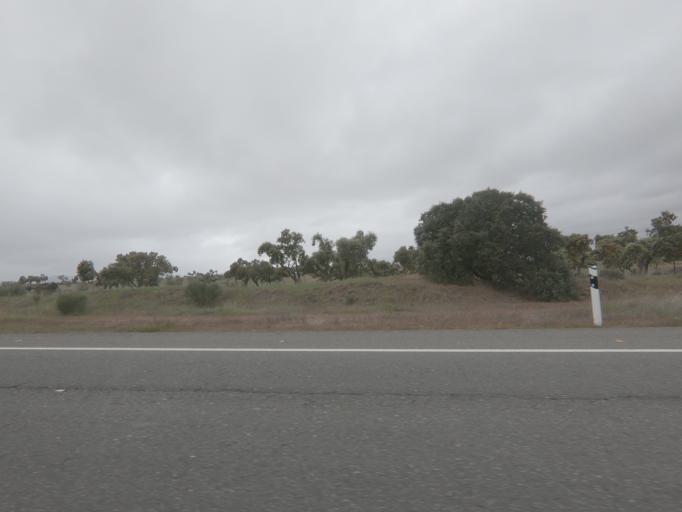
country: ES
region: Extremadura
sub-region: Provincia de Caceres
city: Malpartida de Caceres
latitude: 39.3642
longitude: -6.4610
